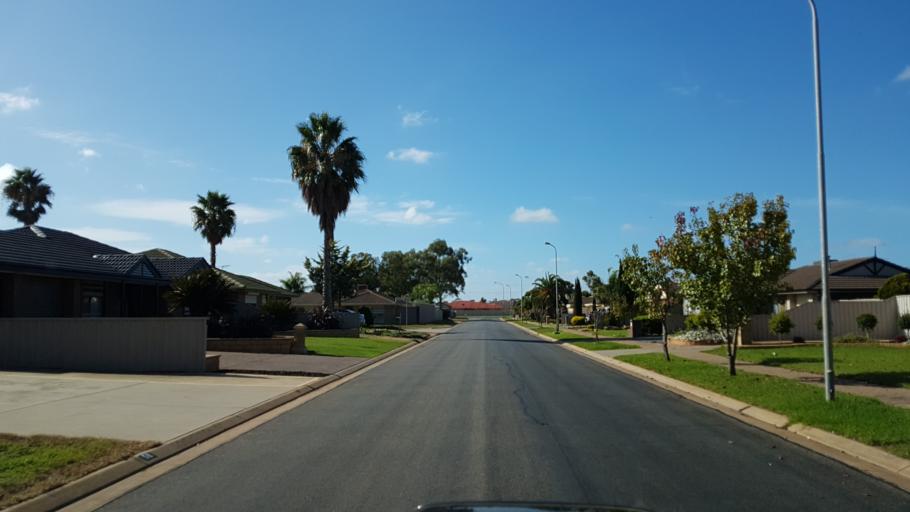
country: AU
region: South Australia
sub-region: Salisbury
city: Salisbury
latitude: -34.7352
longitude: 138.6148
